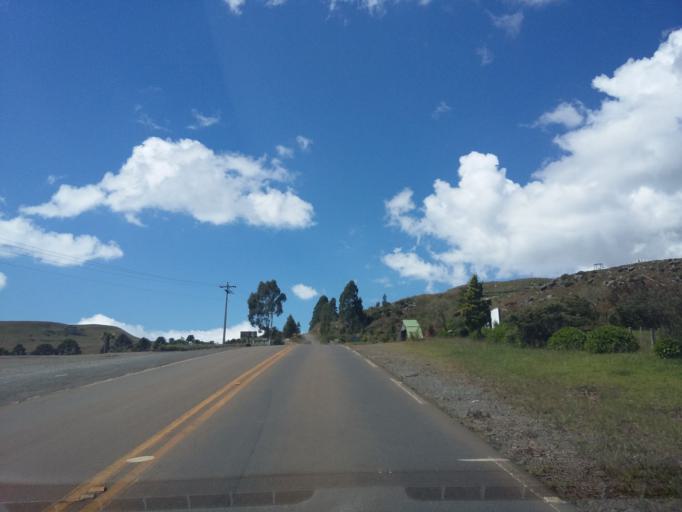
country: BR
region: Santa Catarina
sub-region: Lauro Muller
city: Lauro Muller
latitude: -28.3484
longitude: -49.5996
